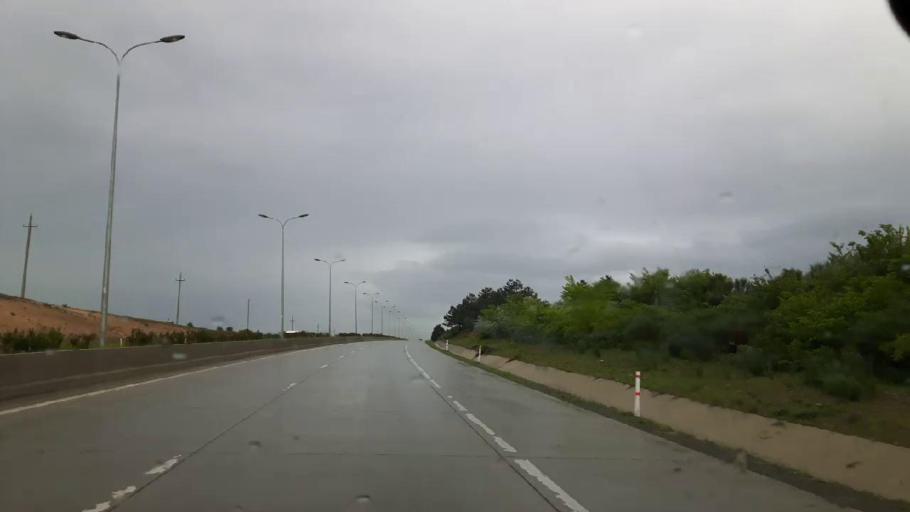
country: GE
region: Shida Kartli
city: Gori
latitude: 42.0186
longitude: 44.0170
